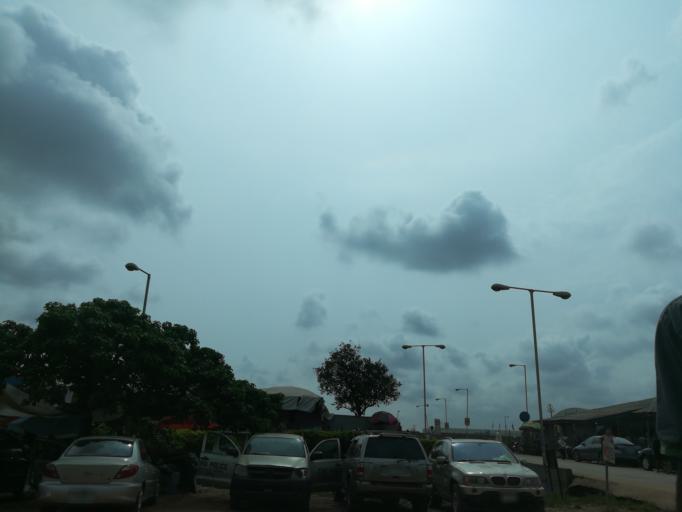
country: NG
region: Lagos
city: Oshodi
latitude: 6.5756
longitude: 3.3235
